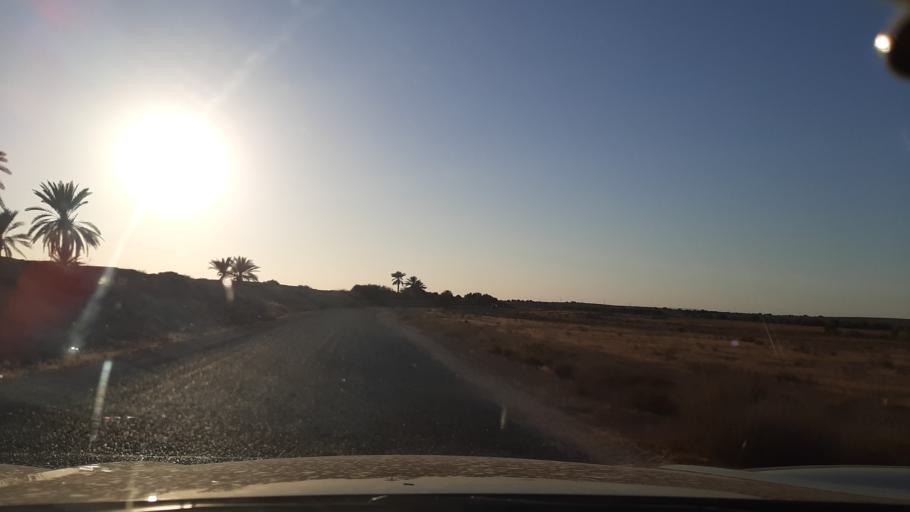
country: TN
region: Qabis
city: Matmata
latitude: 33.6240
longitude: 10.1365
